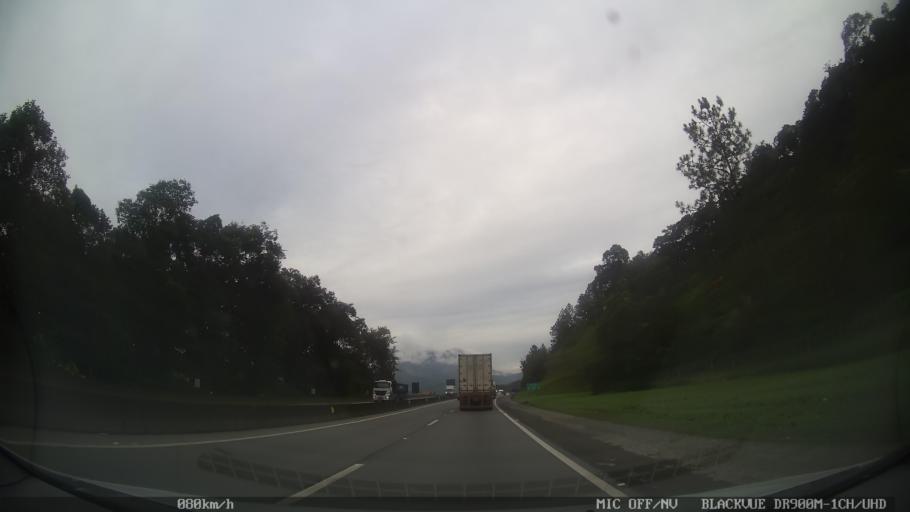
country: BR
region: Santa Catarina
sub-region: Joinville
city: Joinville
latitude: -26.2635
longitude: -48.9013
